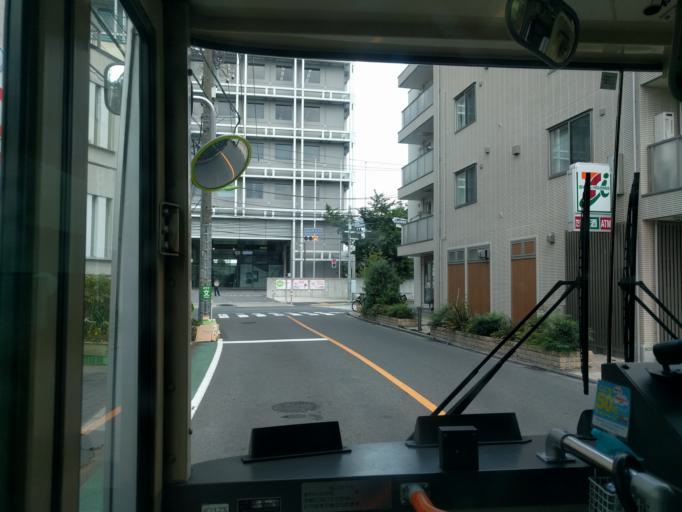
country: JP
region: Tokyo
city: Chofugaoka
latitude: 35.6348
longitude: 139.6161
